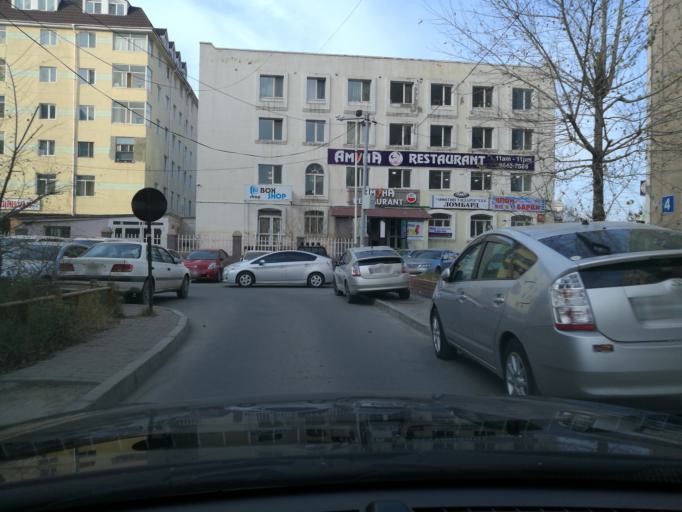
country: MN
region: Ulaanbaatar
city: Ulaanbaatar
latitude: 47.9278
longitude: 106.9262
